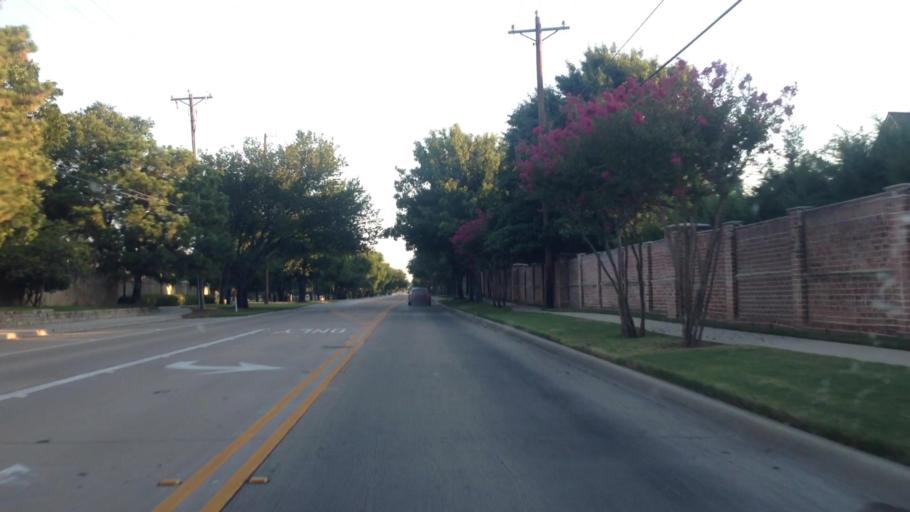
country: US
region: Texas
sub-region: Tarrant County
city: Southlake
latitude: 32.9316
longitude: -97.1336
